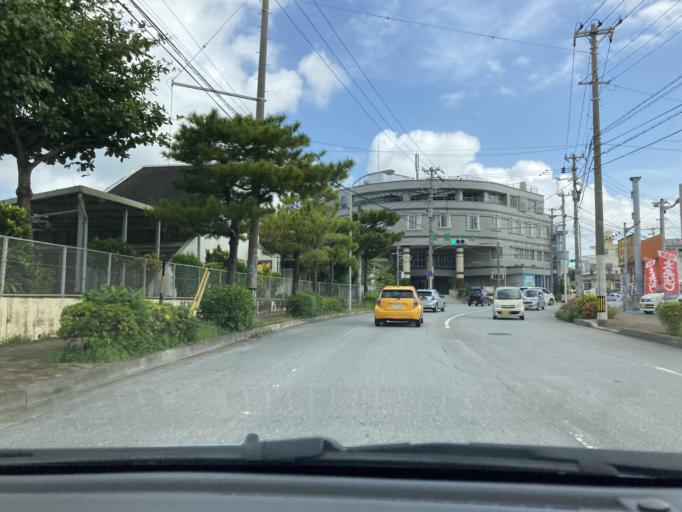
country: JP
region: Okinawa
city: Ginowan
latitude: 26.2617
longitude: 127.7455
